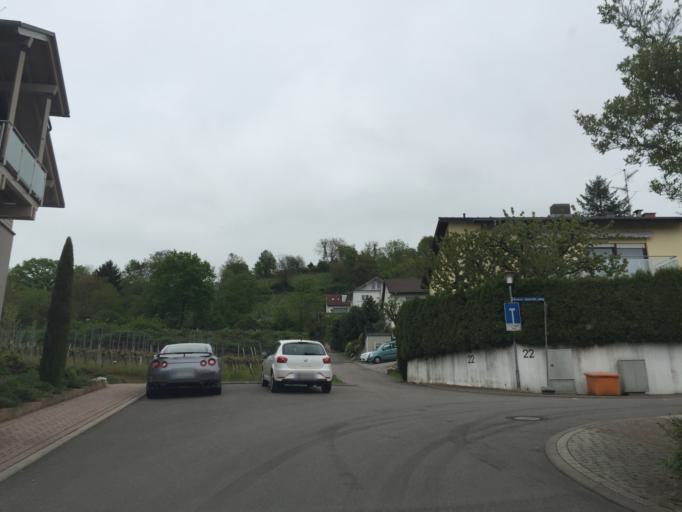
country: DE
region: Baden-Wuerttemberg
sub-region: Karlsruhe Region
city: Schriesheim
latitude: 49.5035
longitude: 8.6671
